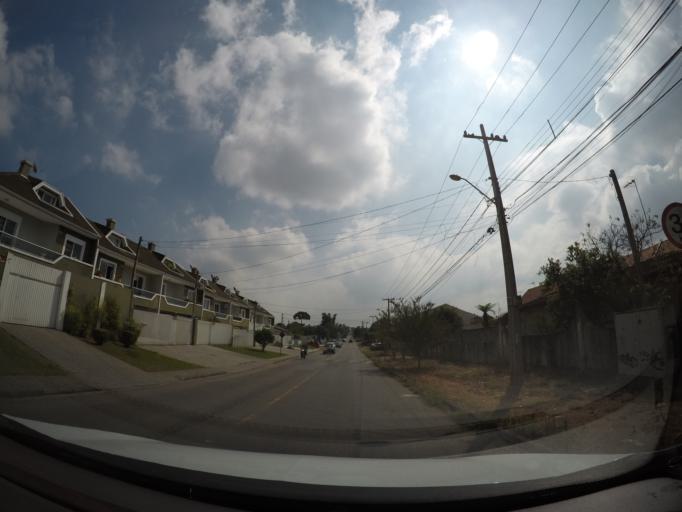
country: BR
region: Parana
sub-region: Sao Jose Dos Pinhais
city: Sao Jose dos Pinhais
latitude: -25.4944
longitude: -49.2535
